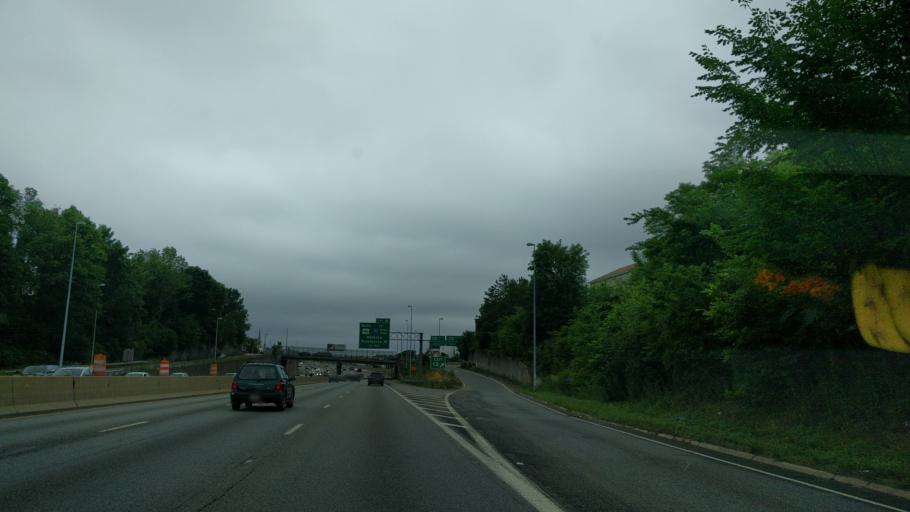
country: US
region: Massachusetts
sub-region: Worcester County
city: Worcester
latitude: 42.2558
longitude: -71.7955
